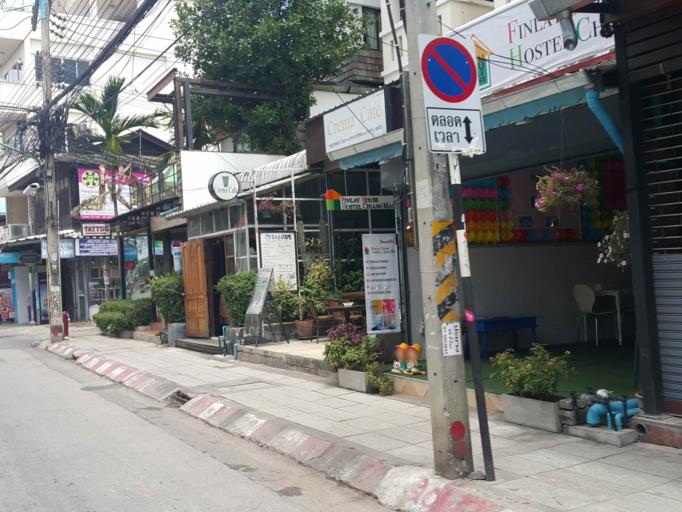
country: TH
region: Chiang Mai
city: Chiang Mai
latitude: 18.7844
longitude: 98.9959
